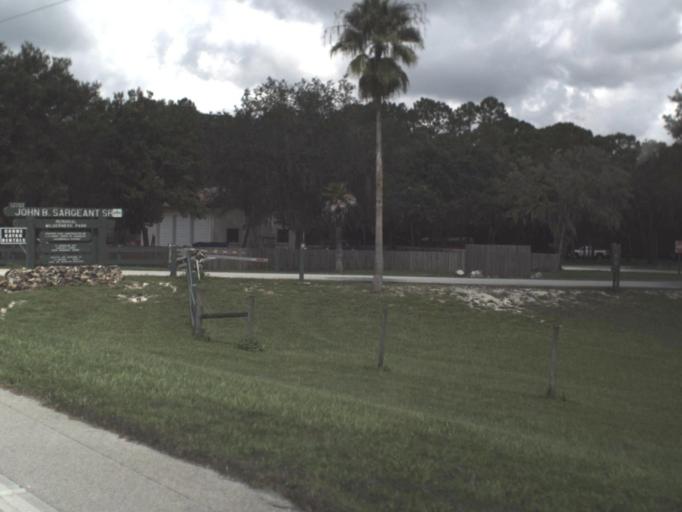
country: US
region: Florida
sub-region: Hillsborough County
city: Thonotosassa
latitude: 28.0796
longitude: -82.2848
